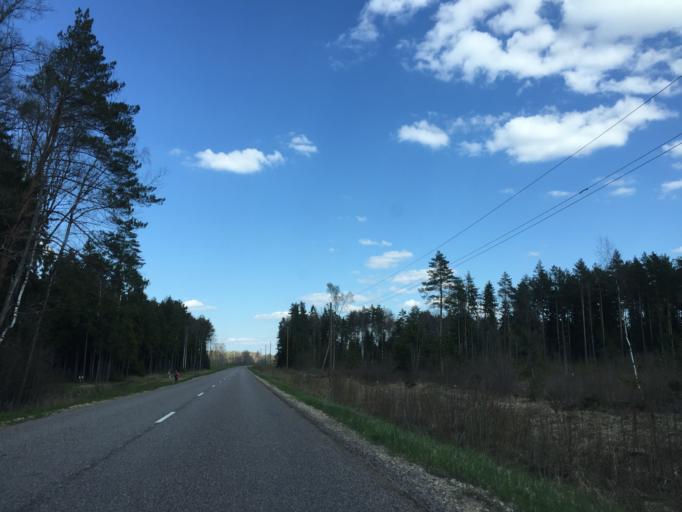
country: LV
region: Saulkrastu
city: Saulkrasti
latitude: 57.2472
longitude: 24.4946
